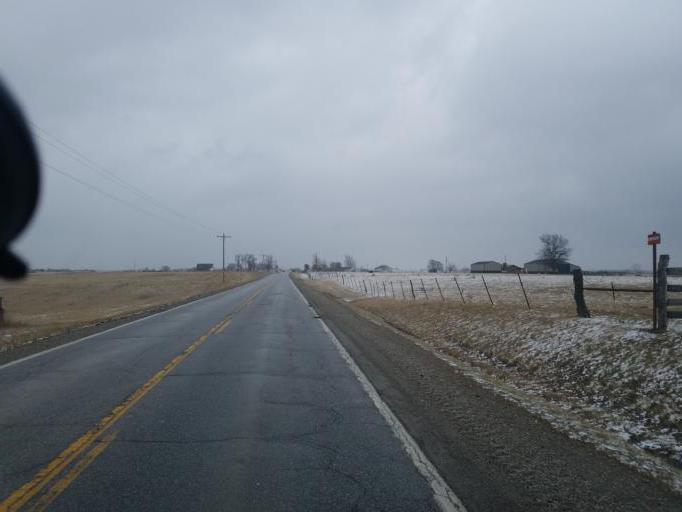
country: US
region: Missouri
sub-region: Putnam County
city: Unionville
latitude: 40.4723
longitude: -92.9665
